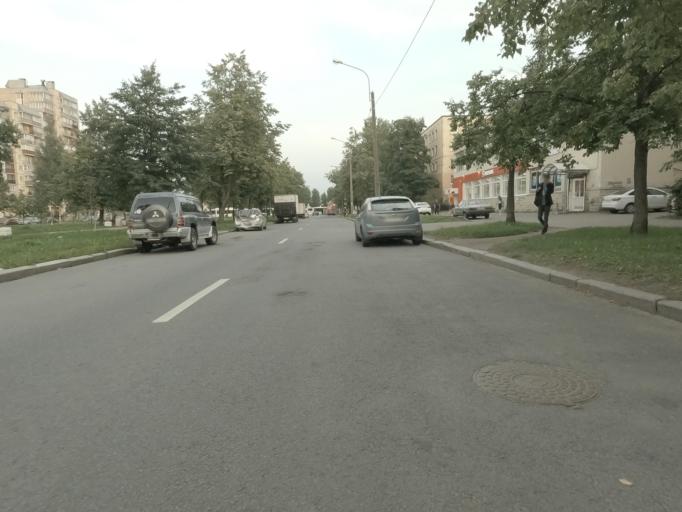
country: RU
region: St.-Petersburg
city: Dachnoye
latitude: 59.8444
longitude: 30.2735
